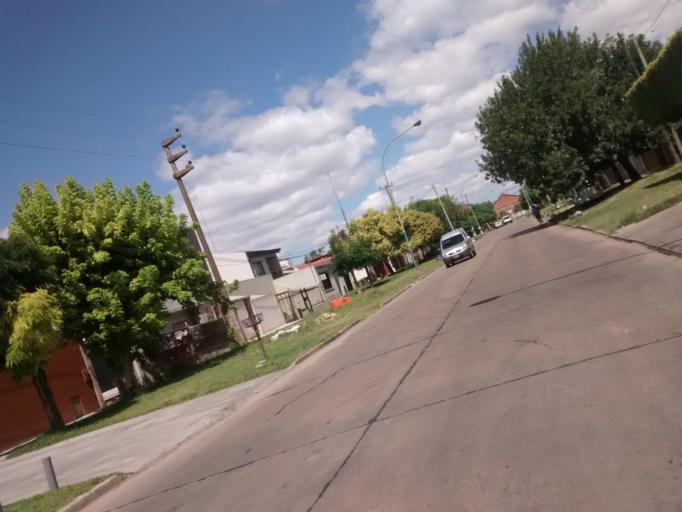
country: AR
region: Buenos Aires
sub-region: Partido de La Plata
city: La Plata
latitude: -34.9426
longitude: -57.9820
